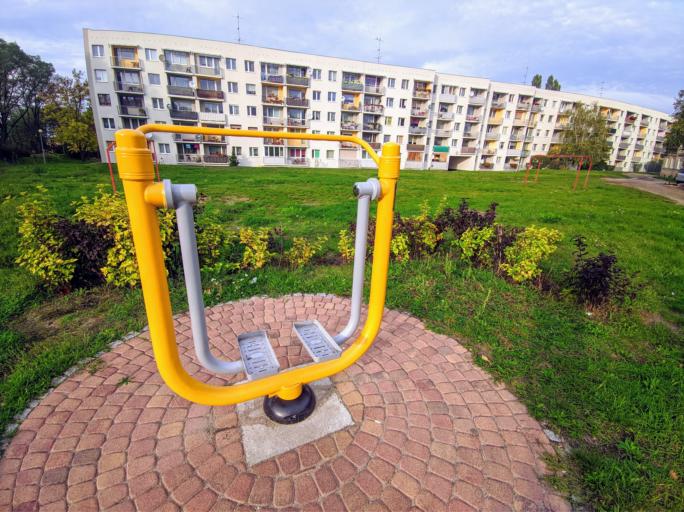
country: PL
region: Lubusz
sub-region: Zielona Gora
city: Zielona Gora
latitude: 51.9378
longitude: 15.4884
